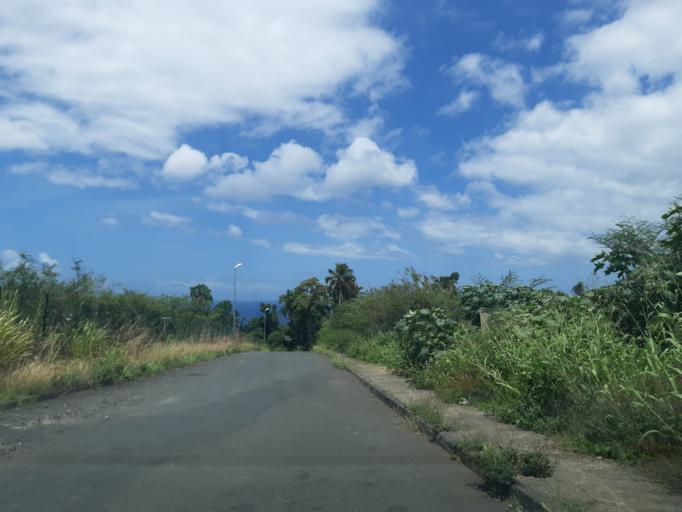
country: GP
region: Guadeloupe
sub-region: Guadeloupe
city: Basse-Terre
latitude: 16.0089
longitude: -61.7153
